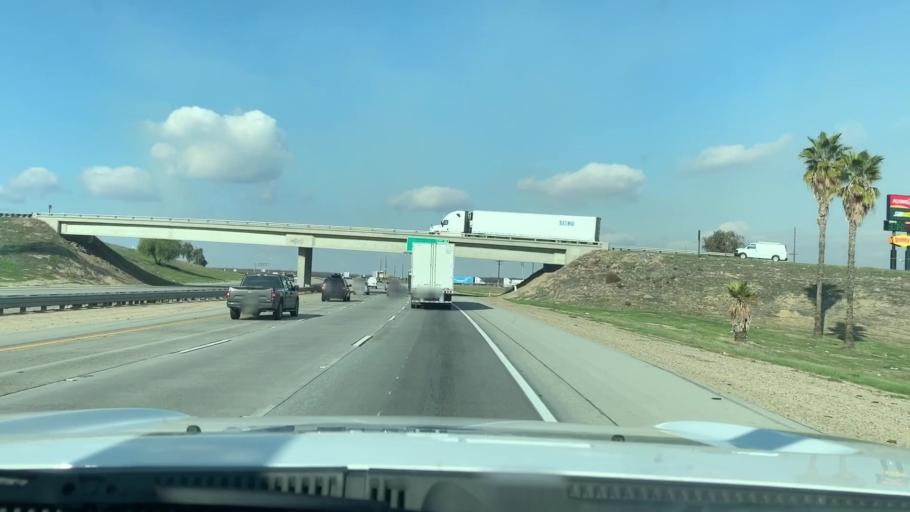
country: US
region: California
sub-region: Kern County
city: Shafter
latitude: 35.5293
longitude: -119.1889
